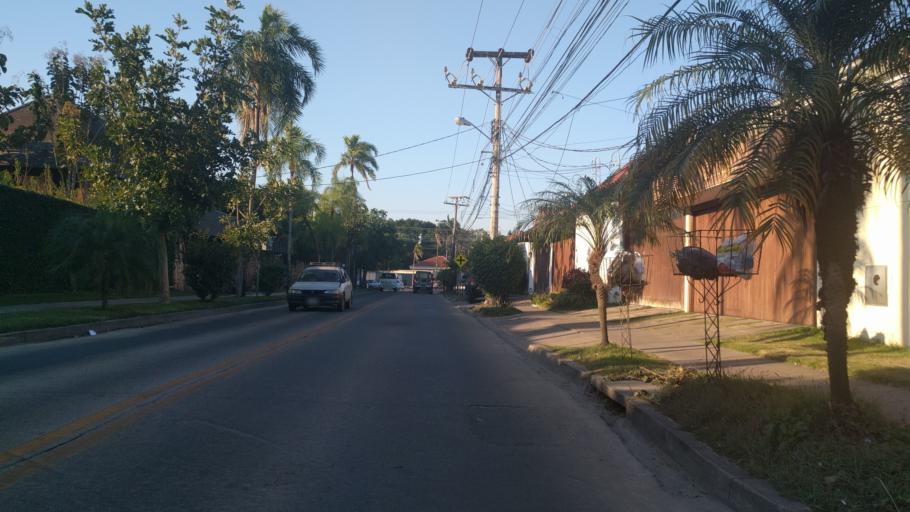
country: BO
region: Santa Cruz
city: Santa Cruz de la Sierra
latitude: -17.8017
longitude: -63.2039
